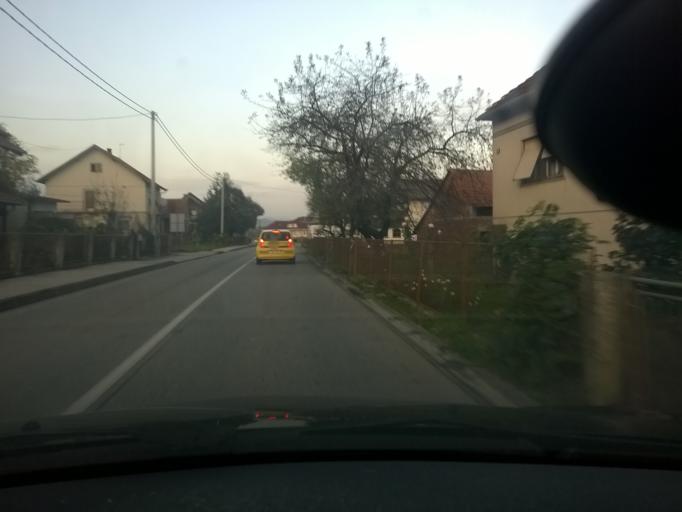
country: HR
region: Krapinsko-Zagorska
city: Zabok
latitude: 46.0579
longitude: 15.9095
